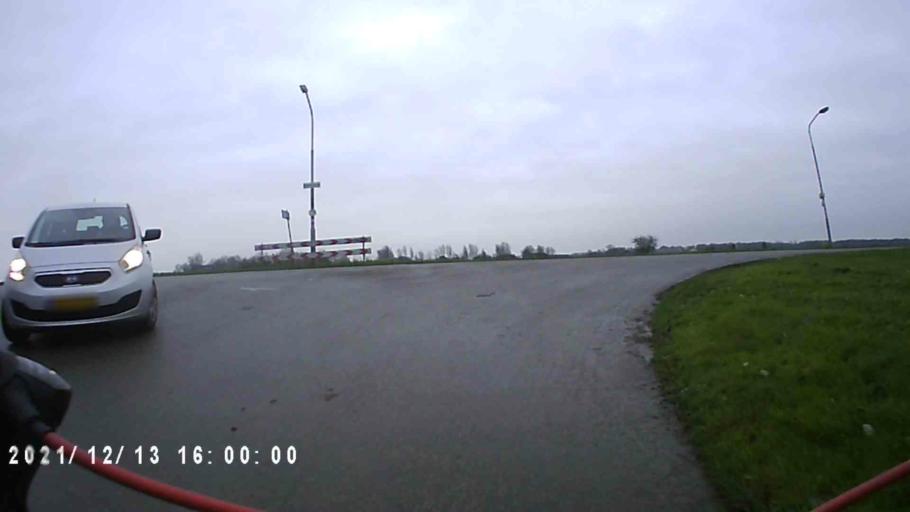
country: NL
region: Groningen
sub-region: Gemeente Appingedam
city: Appingedam
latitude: 53.3387
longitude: 6.8669
